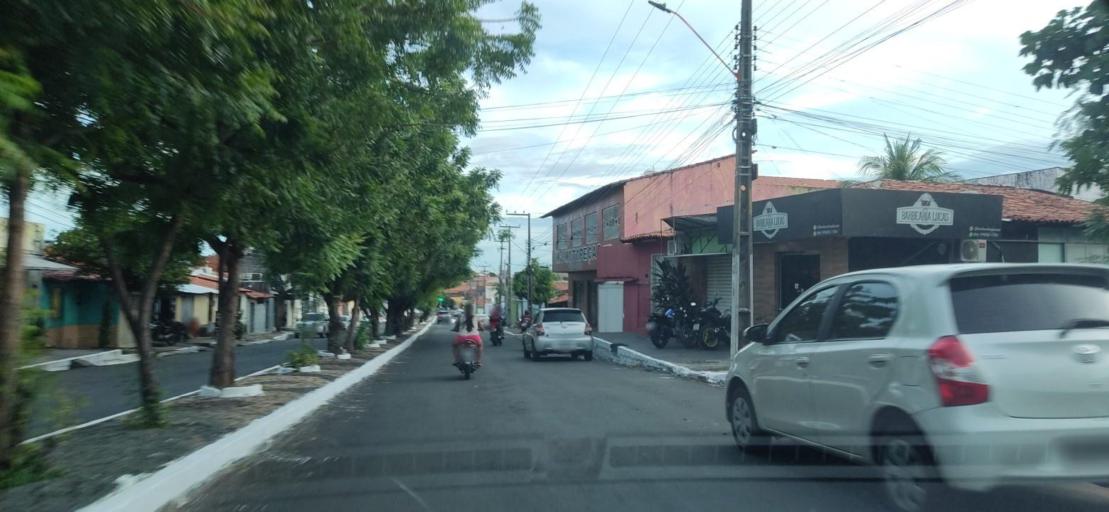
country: BR
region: Piaui
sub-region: Teresina
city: Teresina
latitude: -5.1504
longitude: -42.7876
